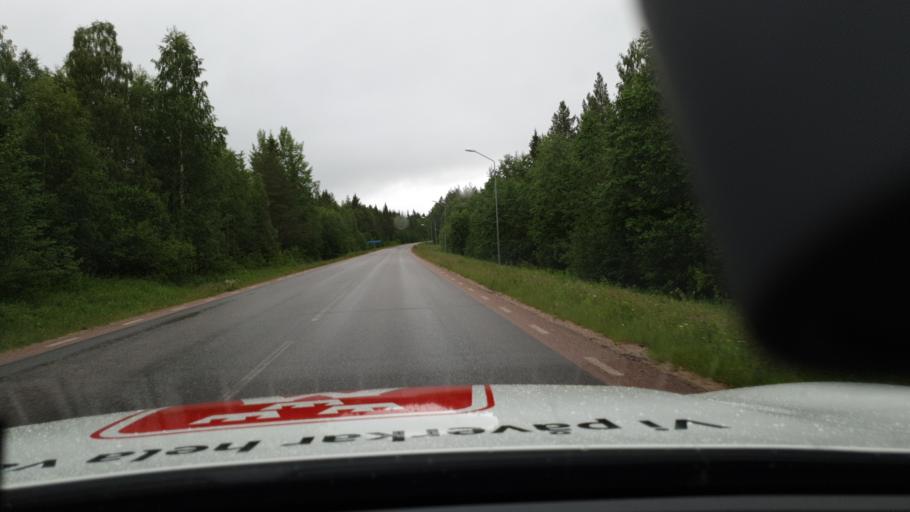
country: SE
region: Norrbotten
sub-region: Overtornea Kommun
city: OEvertornea
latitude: 66.4423
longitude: 23.6178
